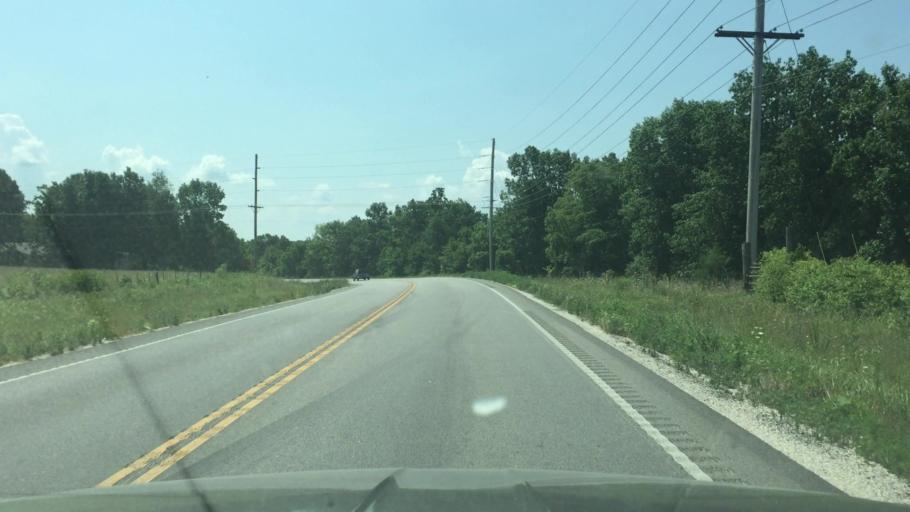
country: US
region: Missouri
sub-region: Miller County
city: Eldon
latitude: 38.3670
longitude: -92.6153
